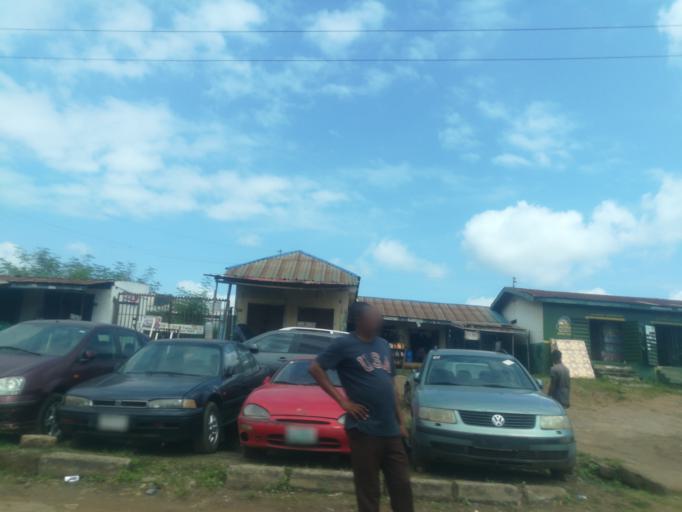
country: NG
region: Oyo
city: Egbeda
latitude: 7.4262
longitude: 3.9932
